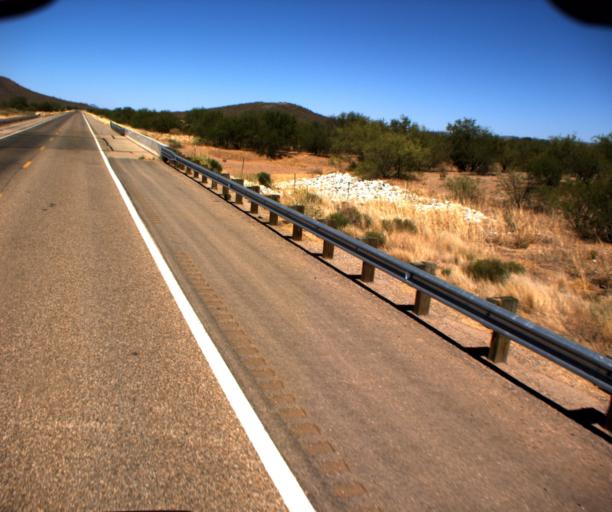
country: US
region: Arizona
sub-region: Pima County
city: Three Points
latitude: 32.0560
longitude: -111.4063
